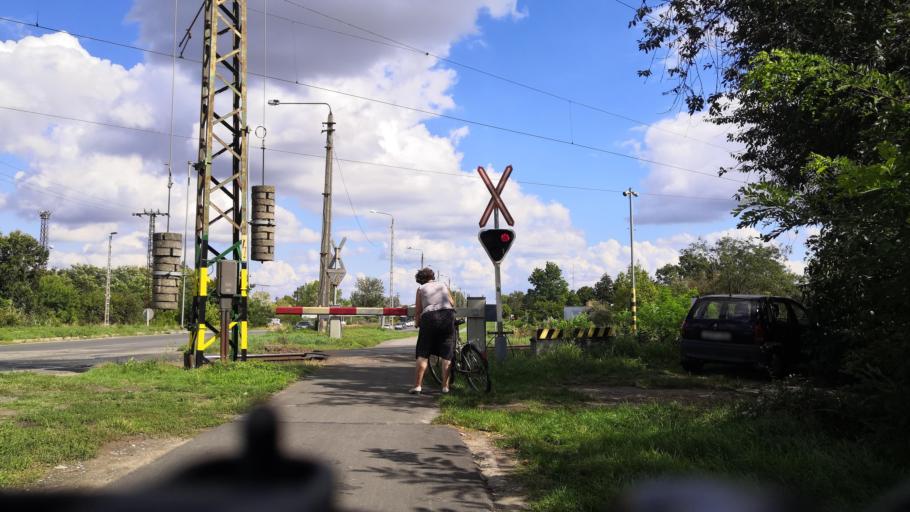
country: HU
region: Csongrad
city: Szeged
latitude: 46.2697
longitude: 20.0919
